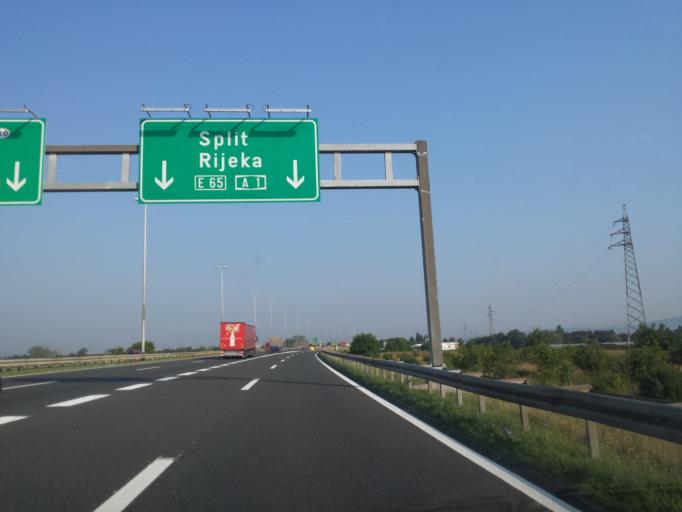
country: HR
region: Grad Zagreb
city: Zadvorsko
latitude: 45.7533
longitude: 15.9069
